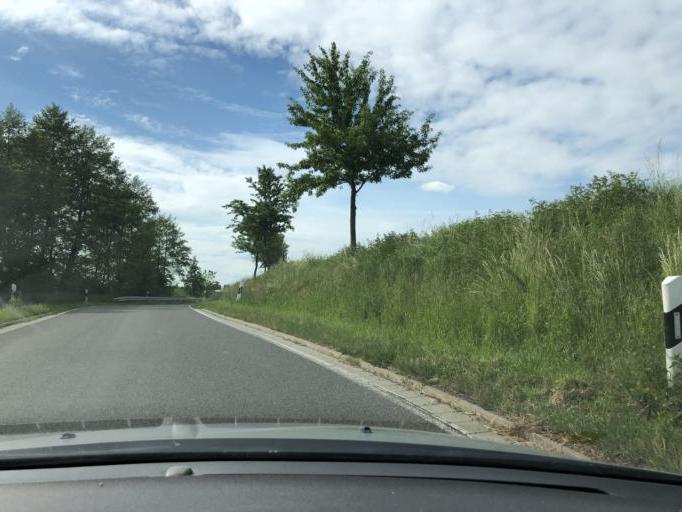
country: DE
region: Saxony
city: Nerchau
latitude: 51.2170
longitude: 12.8106
